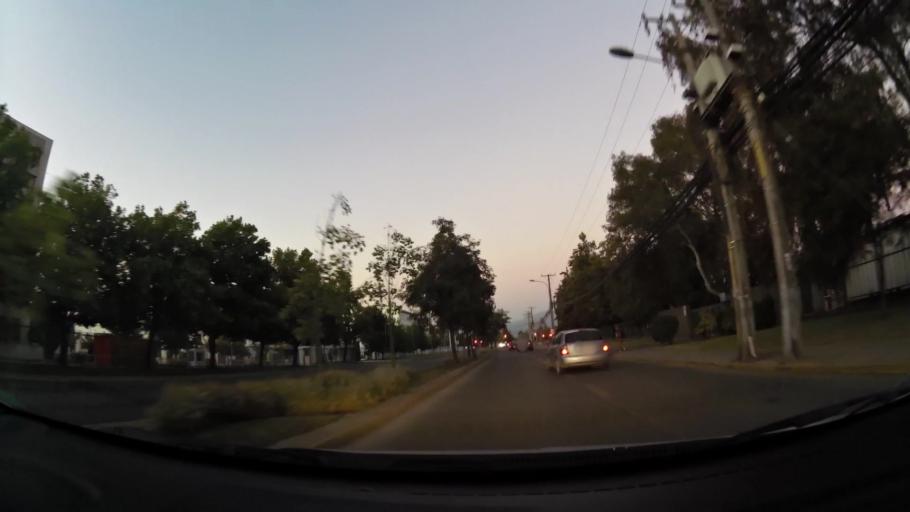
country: CL
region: O'Higgins
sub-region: Provincia de Cachapoal
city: Rancagua
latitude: -34.1870
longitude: -70.7227
